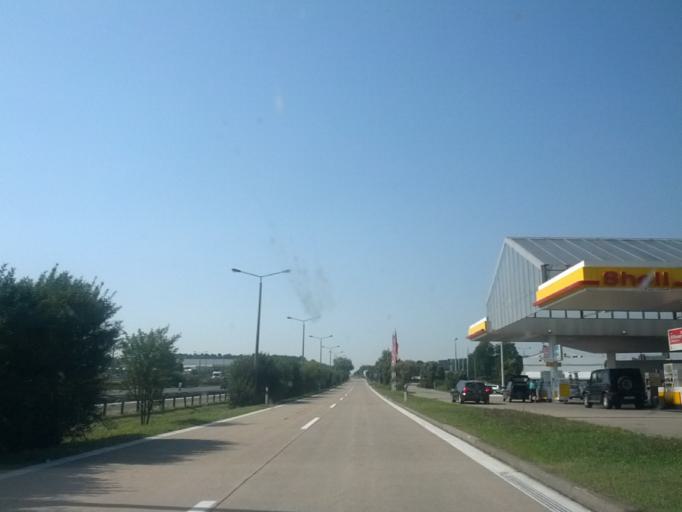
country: DE
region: Brandenburg
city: Linthe
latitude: 52.1344
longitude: 12.7538
